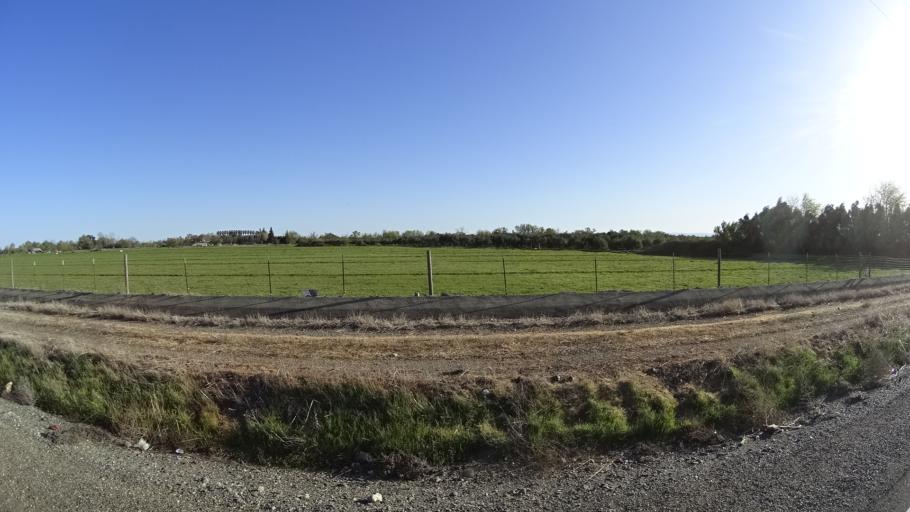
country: US
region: California
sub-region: Glenn County
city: Orland
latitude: 39.7655
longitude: -122.2440
